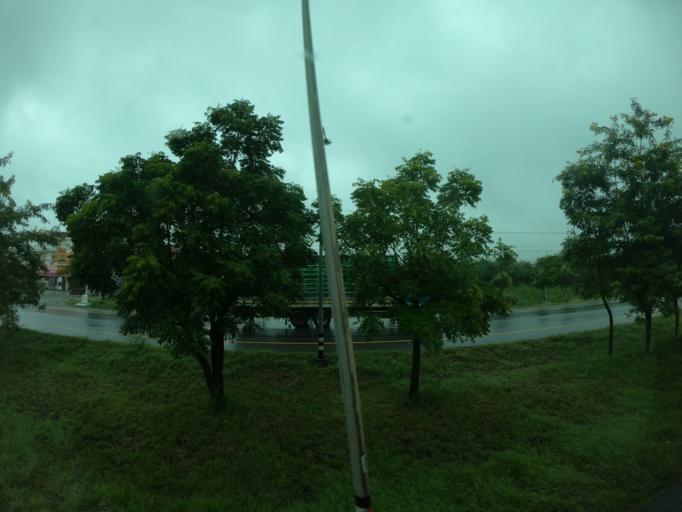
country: TH
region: Nakhon Ratchasima
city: Phimai
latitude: 15.2453
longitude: 102.4173
